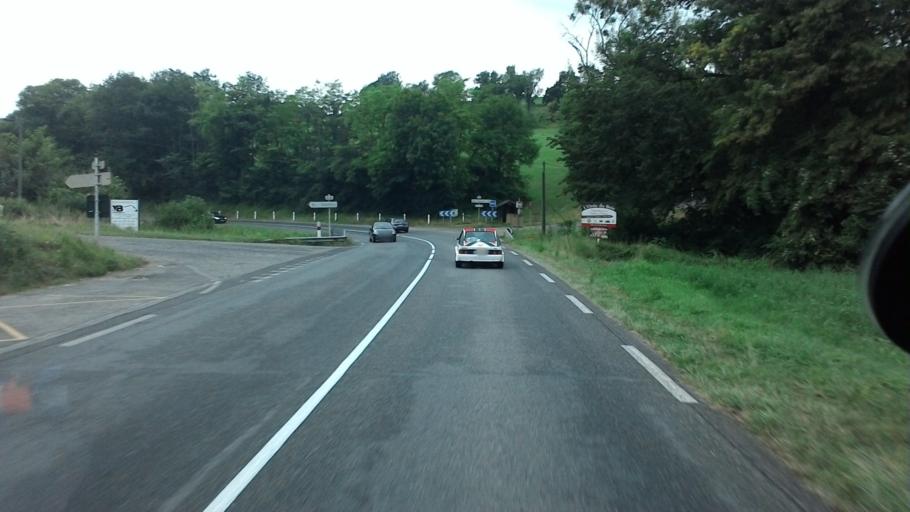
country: FR
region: Rhone-Alpes
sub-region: Departement de la Savoie
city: Yenne
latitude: 45.6968
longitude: 5.8028
